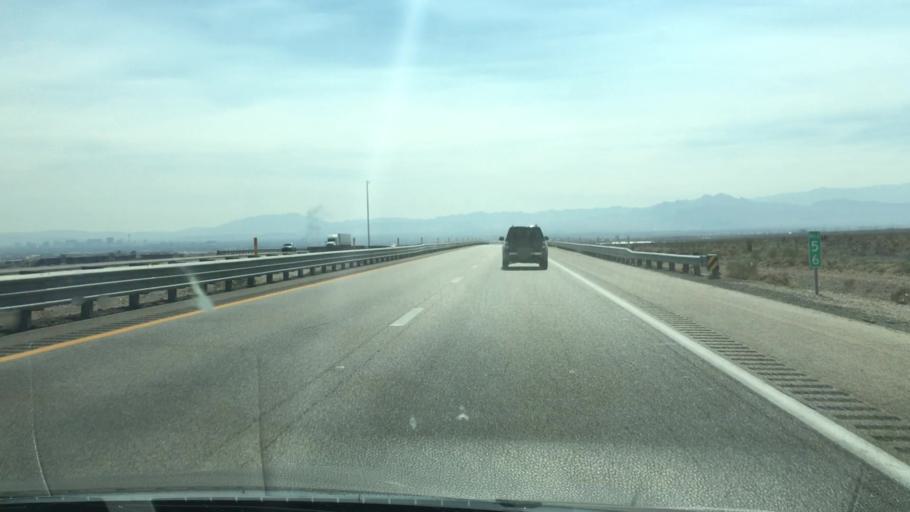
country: US
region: Nevada
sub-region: Clark County
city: Nellis Air Force Base
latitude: 36.2977
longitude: -114.9887
